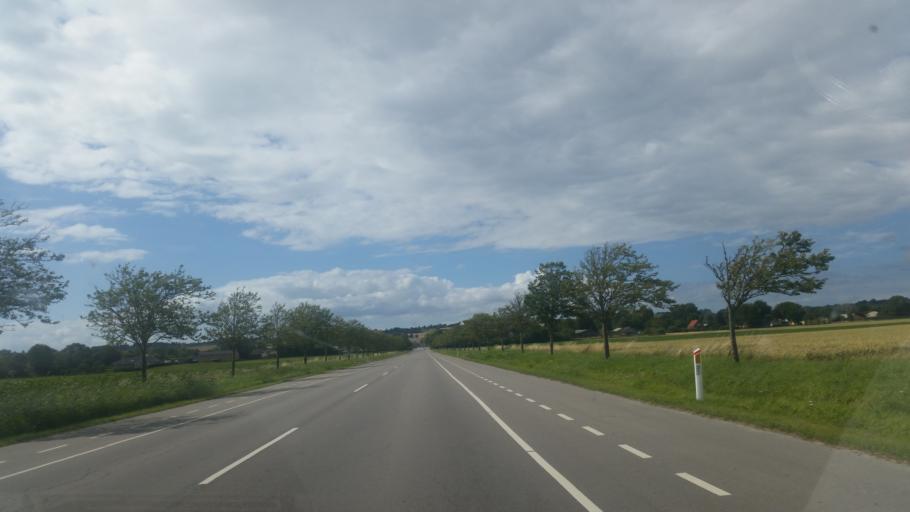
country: DK
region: Zealand
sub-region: Odsherred Kommune
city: Horve
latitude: 55.7966
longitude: 11.4508
